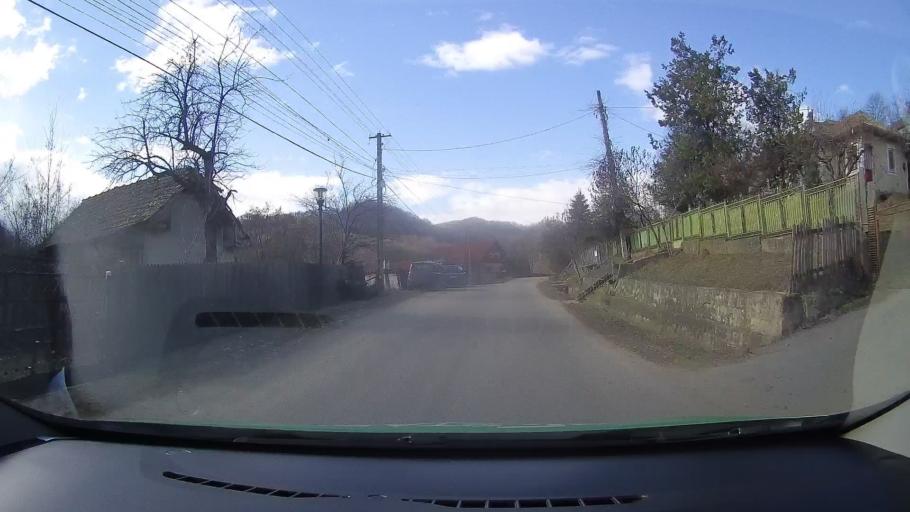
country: RO
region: Dambovita
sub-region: Comuna Varfuri
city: Varfuri
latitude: 45.0881
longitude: 25.5053
